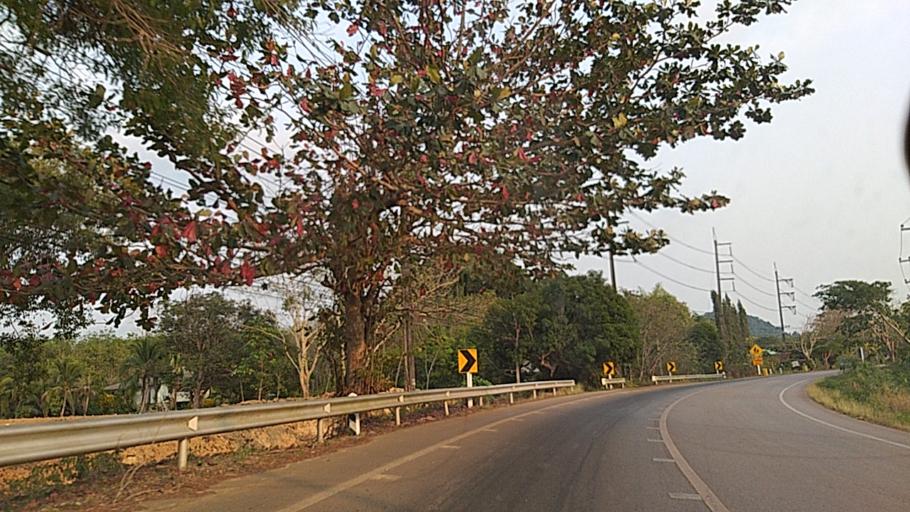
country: TH
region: Trat
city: Laem Ngop
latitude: 12.2319
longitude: 102.3045
